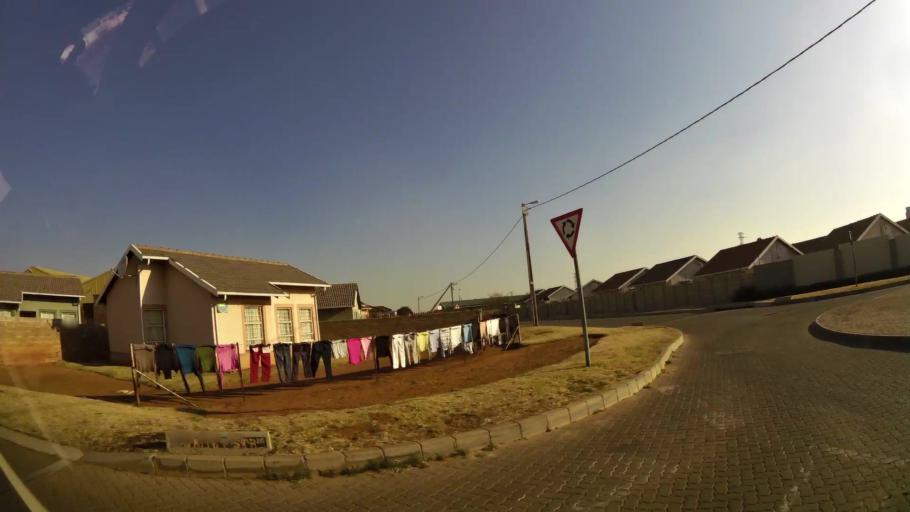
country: ZA
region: Gauteng
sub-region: West Rand District Municipality
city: Randfontein
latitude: -26.1895
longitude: 27.6970
